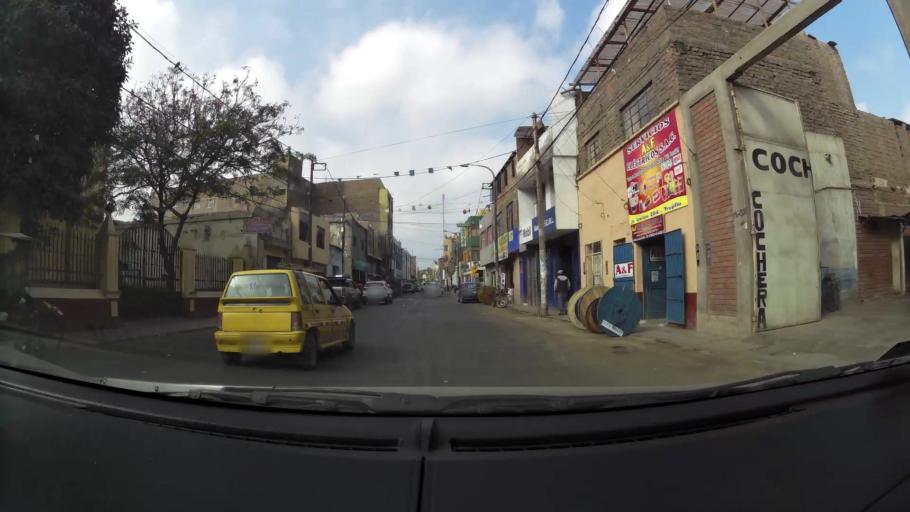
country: PE
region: La Libertad
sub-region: Provincia de Trujillo
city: Trujillo
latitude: -8.1077
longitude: -79.0210
